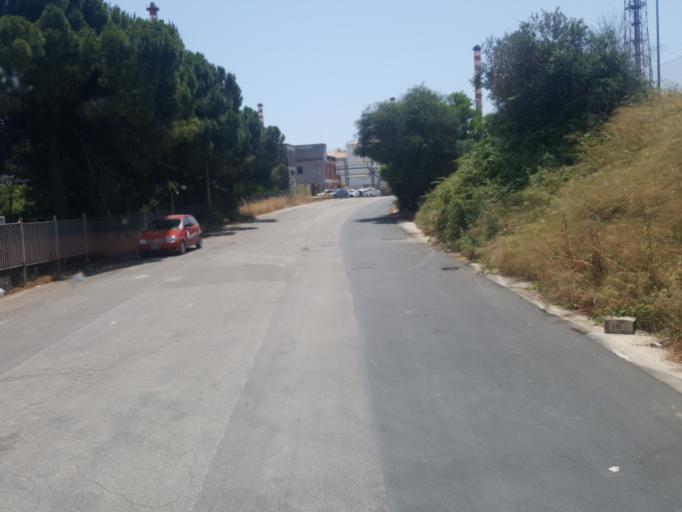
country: IT
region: Apulia
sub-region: Provincia di Taranto
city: Statte
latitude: 40.4975
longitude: 17.1973
